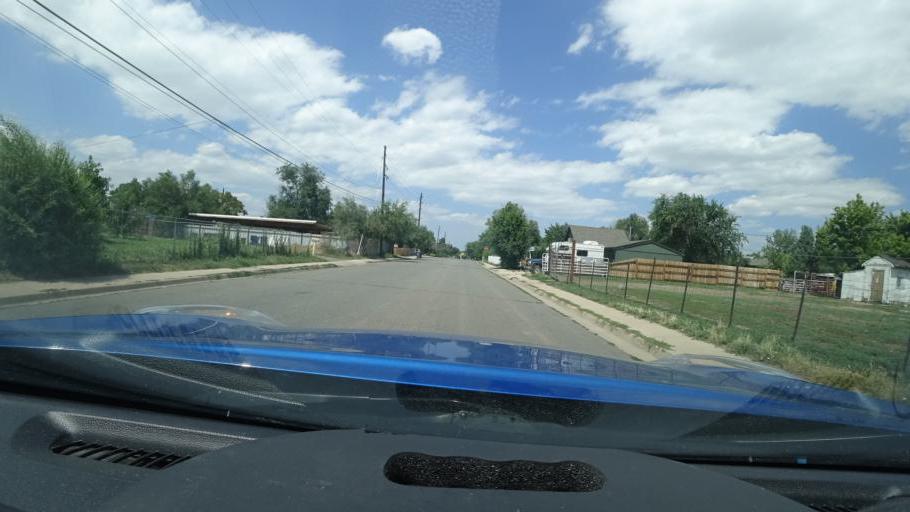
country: US
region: Colorado
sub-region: Arapahoe County
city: Sheridan
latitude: 39.6743
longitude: -105.0227
